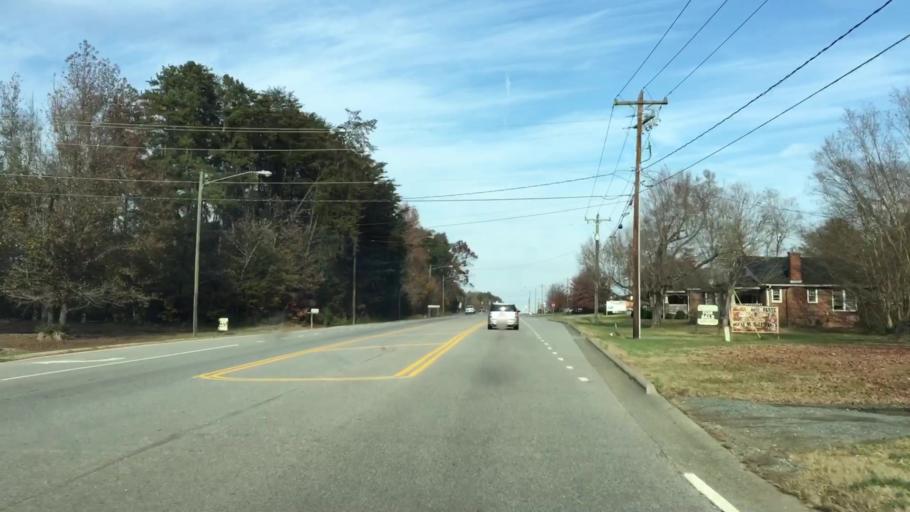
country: US
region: North Carolina
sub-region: Forsyth County
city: Walkertown
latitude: 36.1618
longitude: -80.1406
